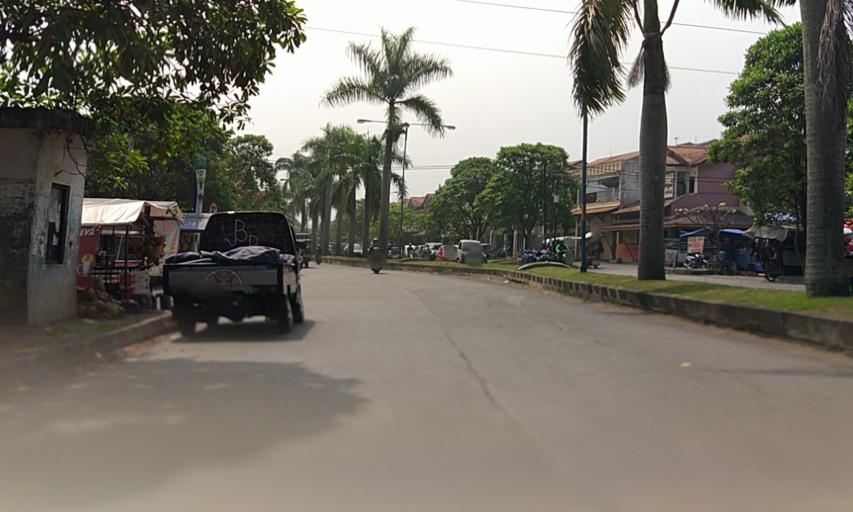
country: ID
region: West Java
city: Margahayukencana
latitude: -6.9583
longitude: 107.5609
